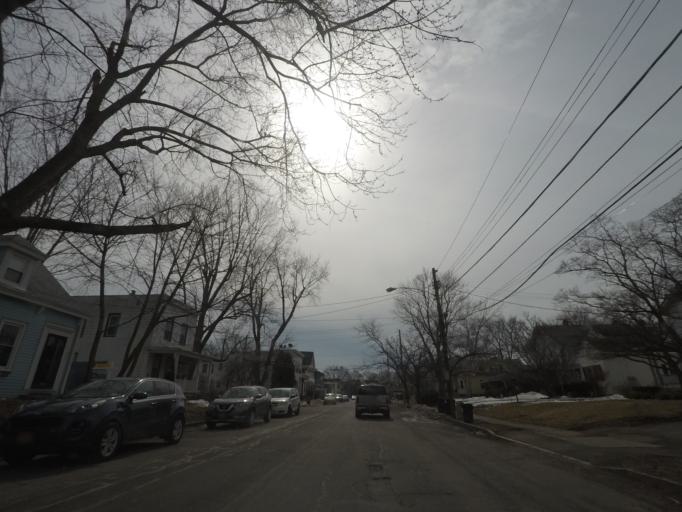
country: US
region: New York
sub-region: Albany County
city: West Albany
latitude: 42.6548
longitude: -73.7880
